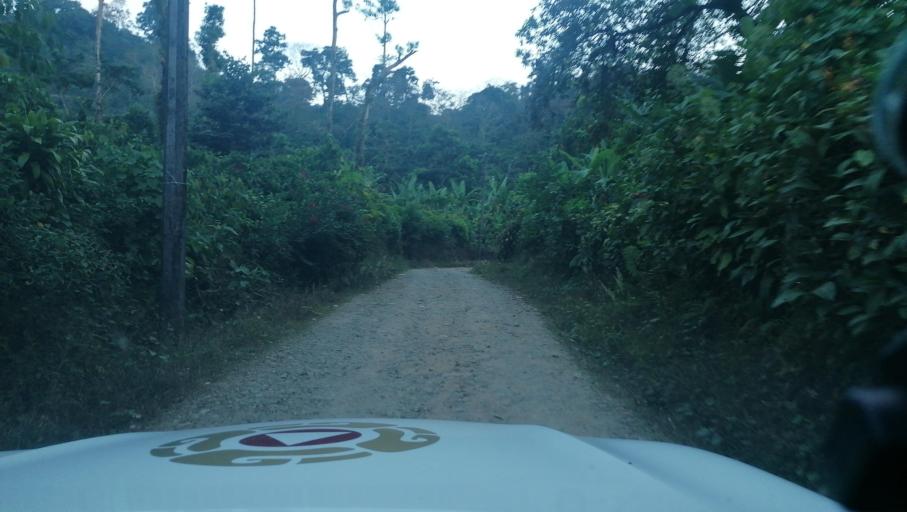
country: MX
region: Chiapas
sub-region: Cacahoatan
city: Benito Juarez
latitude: 15.0748
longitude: -92.2268
